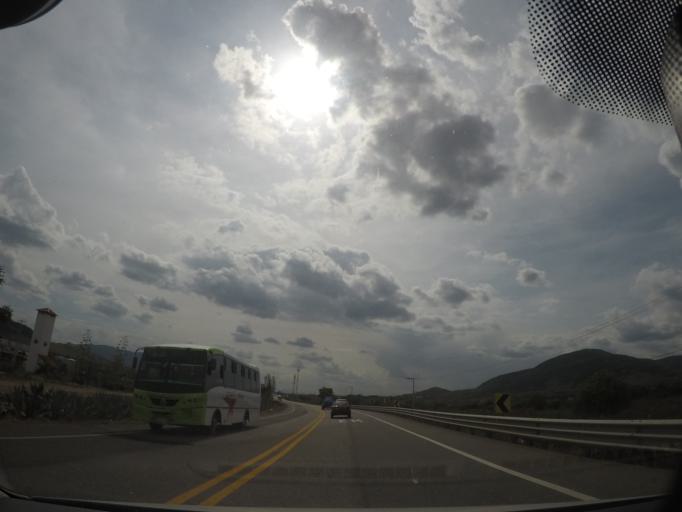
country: MX
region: Oaxaca
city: San Jeronimo Tlacochahuaya
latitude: 17.0181
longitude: -96.5652
